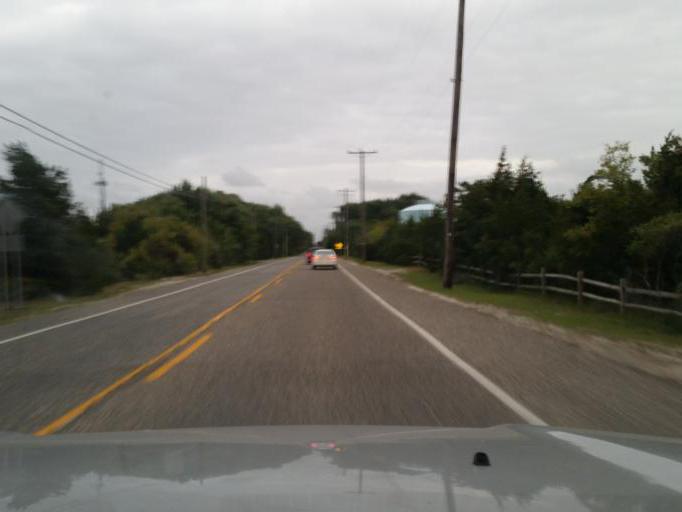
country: US
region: New Jersey
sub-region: Cape May County
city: West Cape May
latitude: 38.9436
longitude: -74.9662
